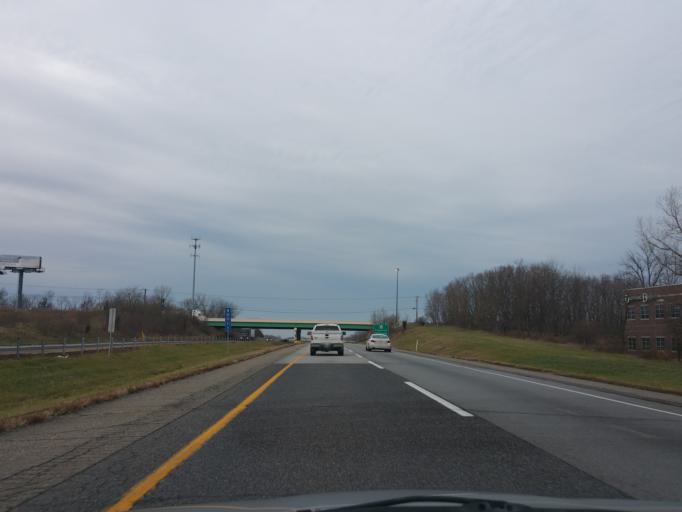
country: US
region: Indiana
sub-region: Porter County
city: Chesterton
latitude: 41.5730
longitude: -87.0424
